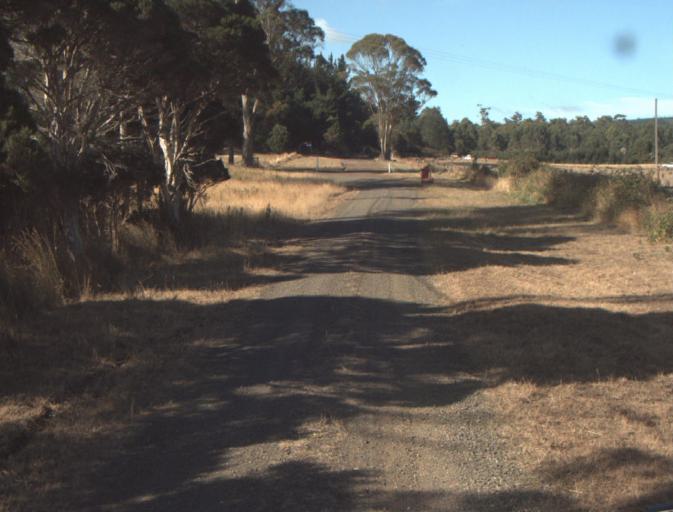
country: AU
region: Tasmania
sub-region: Dorset
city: Bridport
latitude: -41.1434
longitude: 147.2123
